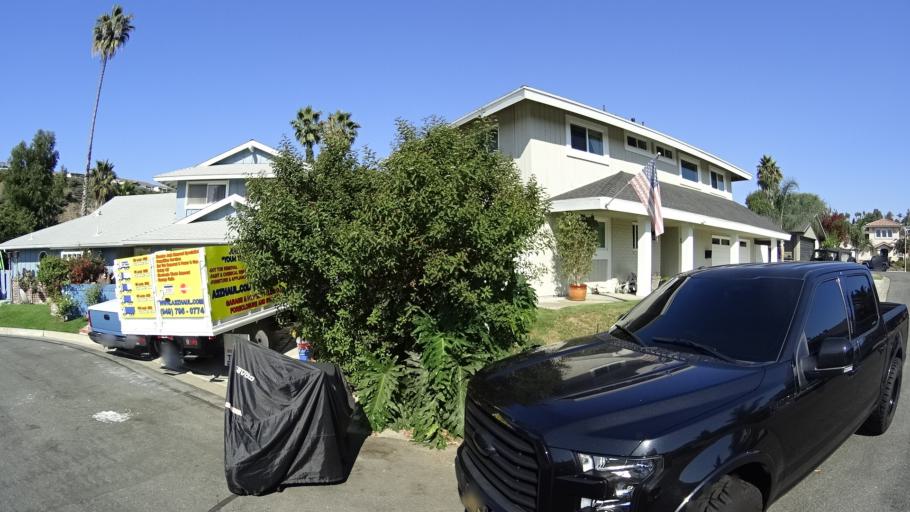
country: US
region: California
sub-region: Orange County
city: San Clemente
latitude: 33.4450
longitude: -117.6434
